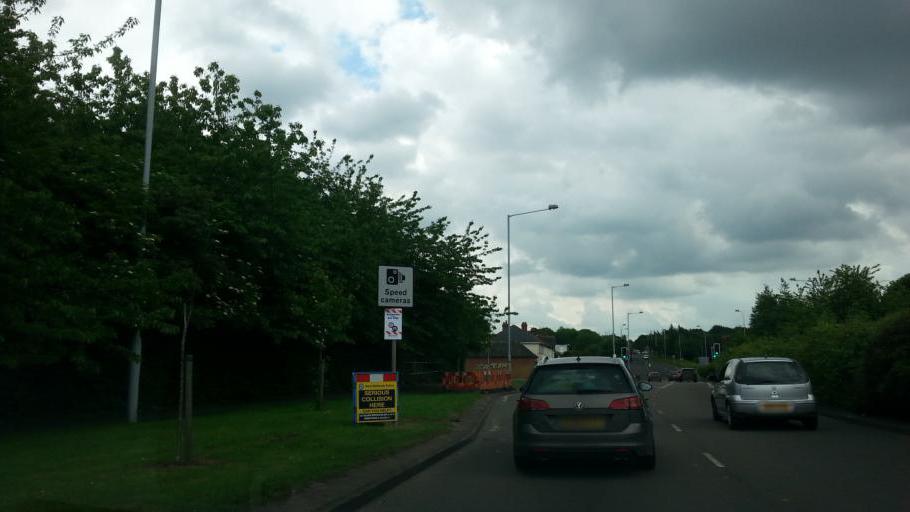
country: GB
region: England
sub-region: Wolverhampton
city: Bilston
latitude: 52.5519
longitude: -2.0967
